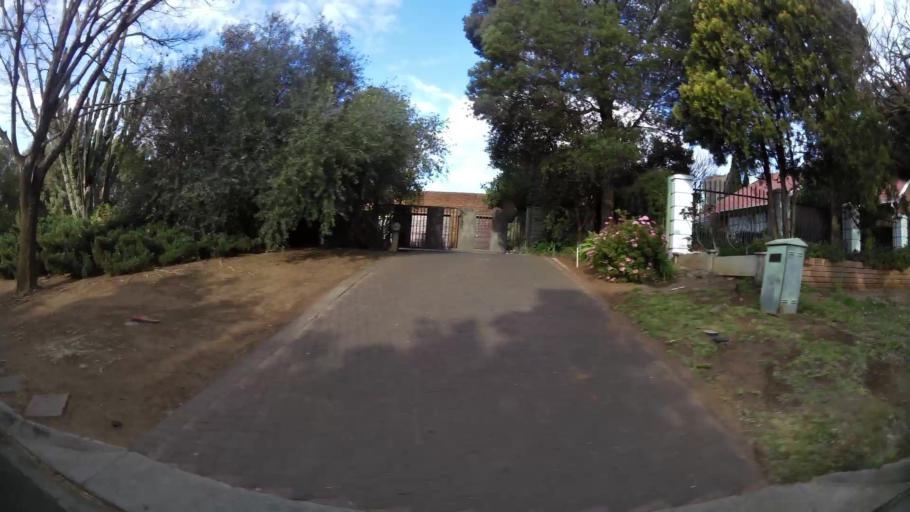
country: ZA
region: Orange Free State
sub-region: Mangaung Metropolitan Municipality
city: Bloemfontein
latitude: -29.0767
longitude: 26.2066
